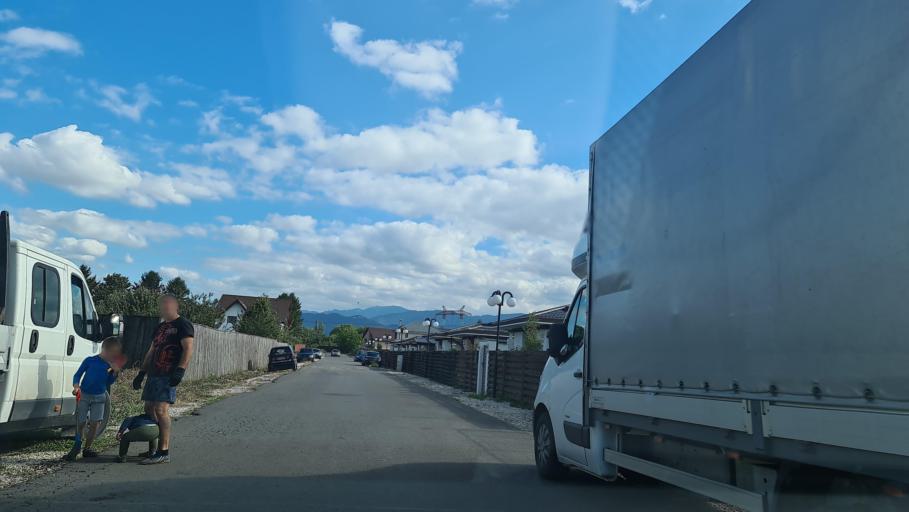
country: RO
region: Brasov
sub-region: Comuna Ghimbav
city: Ghimbav
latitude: 45.6978
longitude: 25.5487
